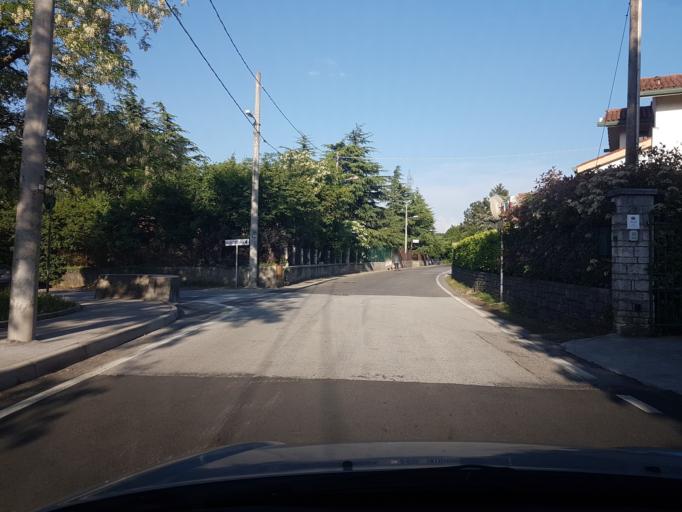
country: IT
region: Friuli Venezia Giulia
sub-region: Provincia di Trieste
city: Villa Opicina
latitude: 45.6887
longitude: 13.7764
